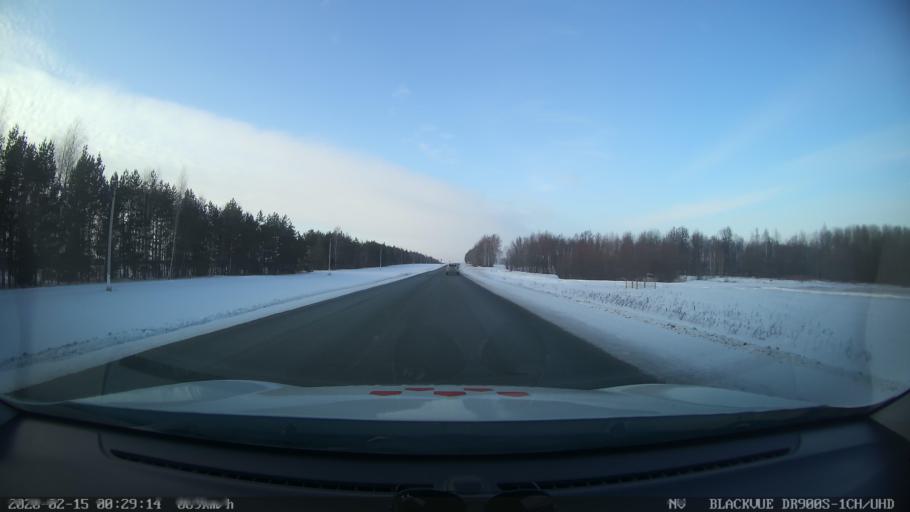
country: RU
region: Tatarstan
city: Verkhniy Uslon
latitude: 55.6490
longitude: 48.8705
